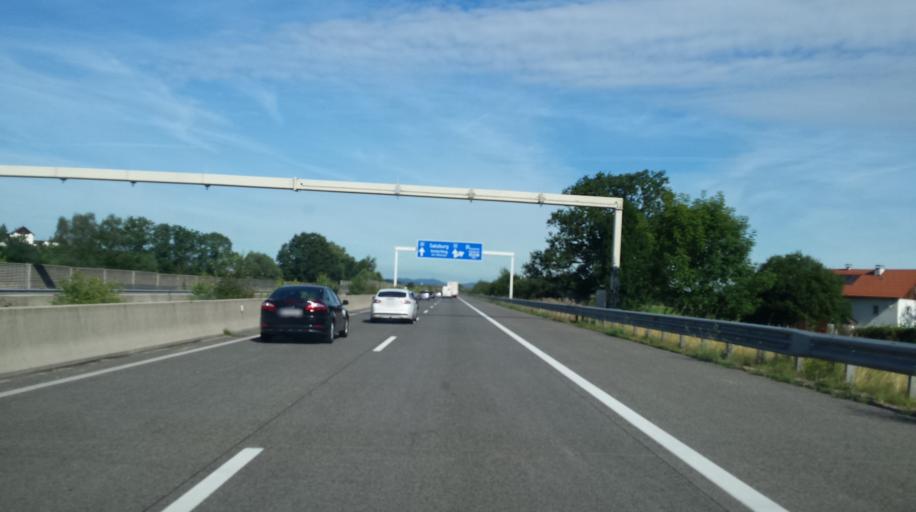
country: AT
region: Upper Austria
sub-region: Politischer Bezirk Vocklabruck
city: Aurach am Hongar
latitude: 47.9532
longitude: 13.6619
